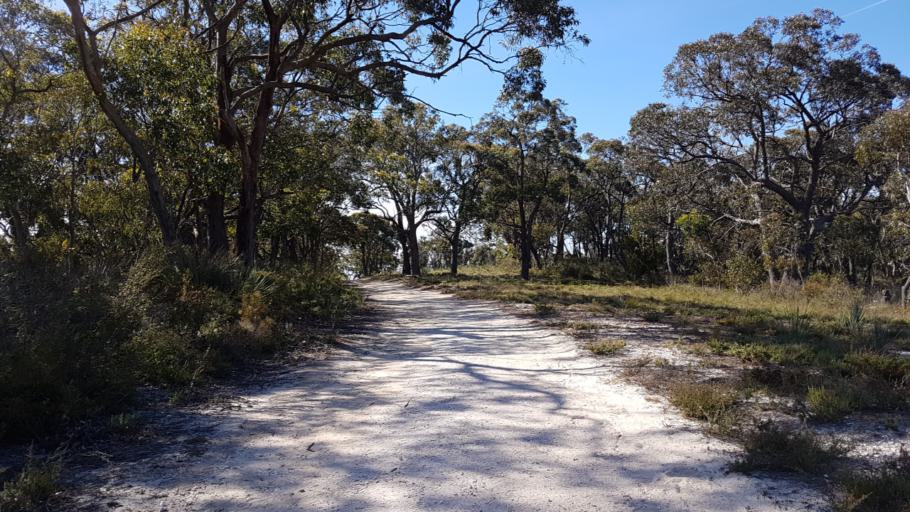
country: AU
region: South Australia
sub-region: Adelaide Hills
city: Adelaide Hills
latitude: -34.8995
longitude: 138.7224
